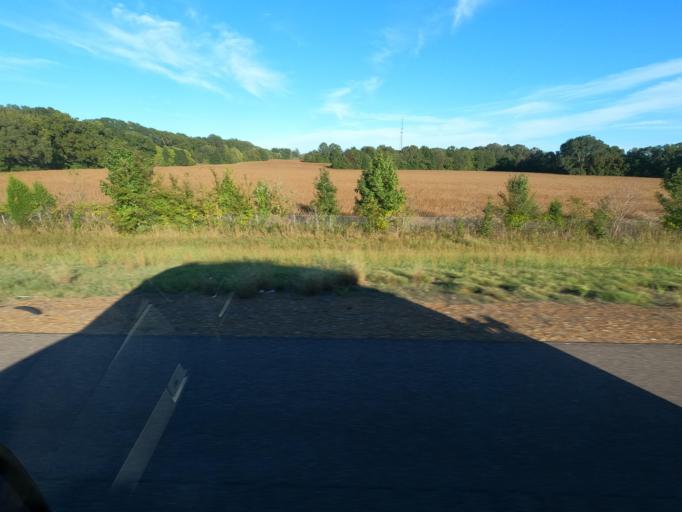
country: US
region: Tennessee
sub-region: Fayette County
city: Piperton
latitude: 35.1011
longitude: -89.6369
